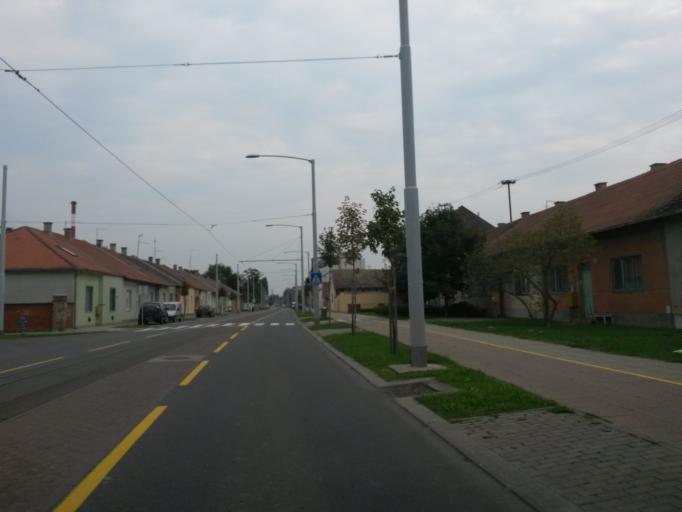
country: HR
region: Osjecko-Baranjska
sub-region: Grad Osijek
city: Osijek
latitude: 45.5499
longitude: 18.7197
